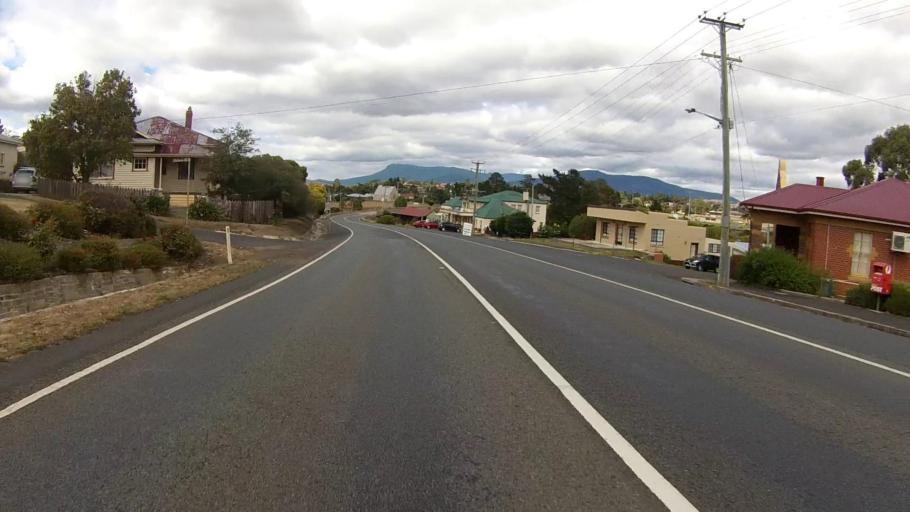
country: AU
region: Tasmania
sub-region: Brighton
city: Bridgewater
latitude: -42.6834
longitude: 147.2658
